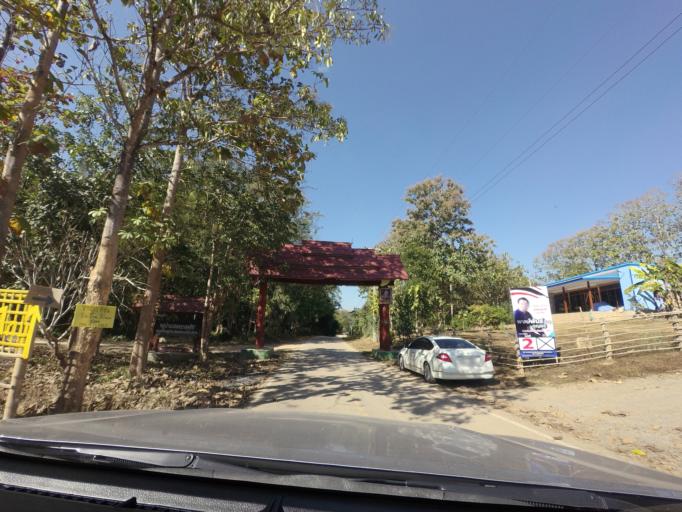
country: TH
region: Lampang
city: Chae Hom
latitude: 18.5949
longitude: 99.6270
